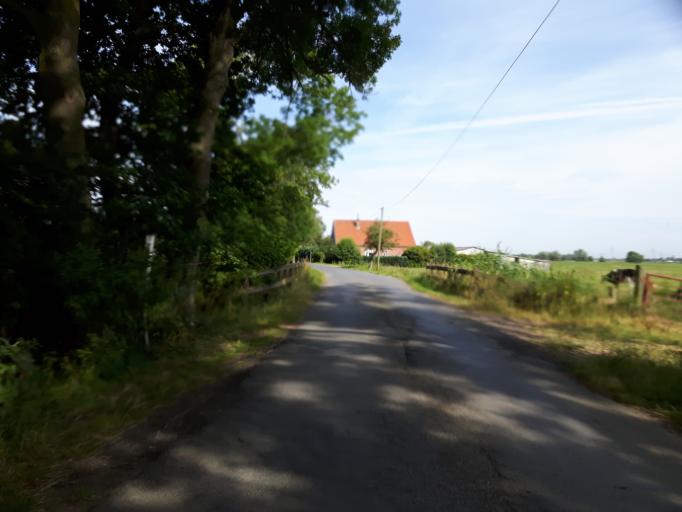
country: DE
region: Lower Saxony
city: Neuenkirchen
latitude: 53.1757
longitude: 8.5051
